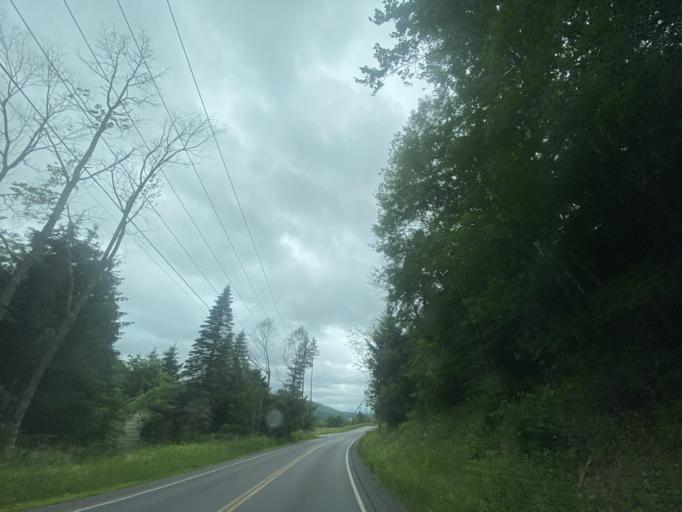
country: US
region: New York
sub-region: Schoharie County
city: Middleburgh
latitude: 42.3890
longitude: -74.3246
